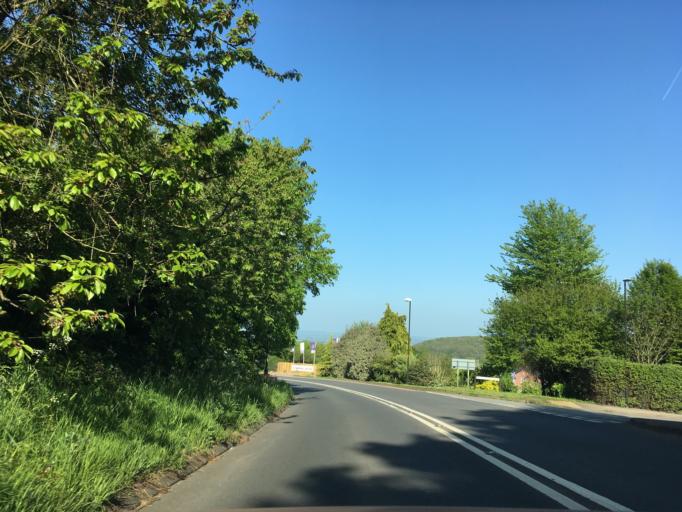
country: GB
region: Wales
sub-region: Monmouthshire
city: Chepstow
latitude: 51.6492
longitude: -2.6611
